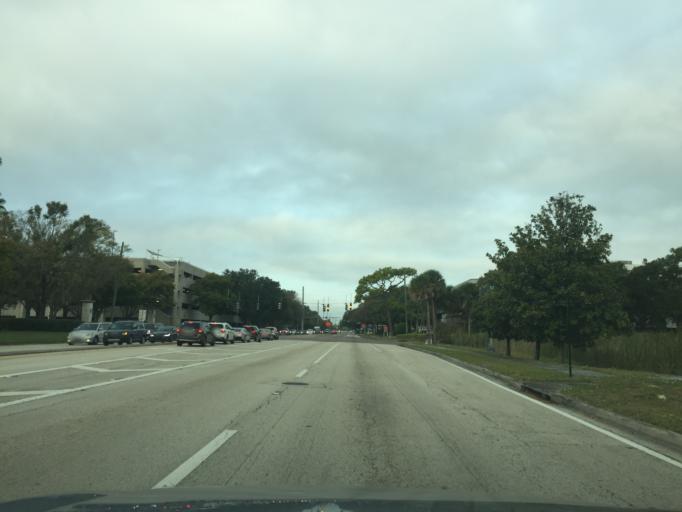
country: US
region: Florida
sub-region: Hillsborough County
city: Town 'n' Country
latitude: 27.9818
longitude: -82.5478
